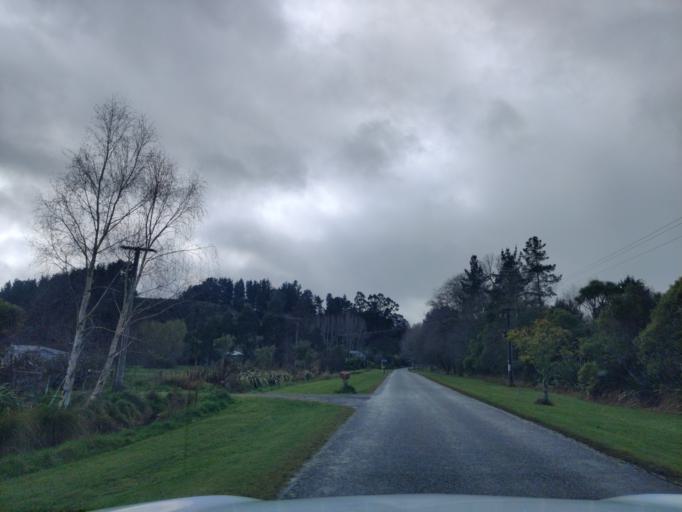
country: NZ
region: Manawatu-Wanganui
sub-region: Palmerston North City
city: Palmerston North
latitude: -40.1698
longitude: 175.7998
